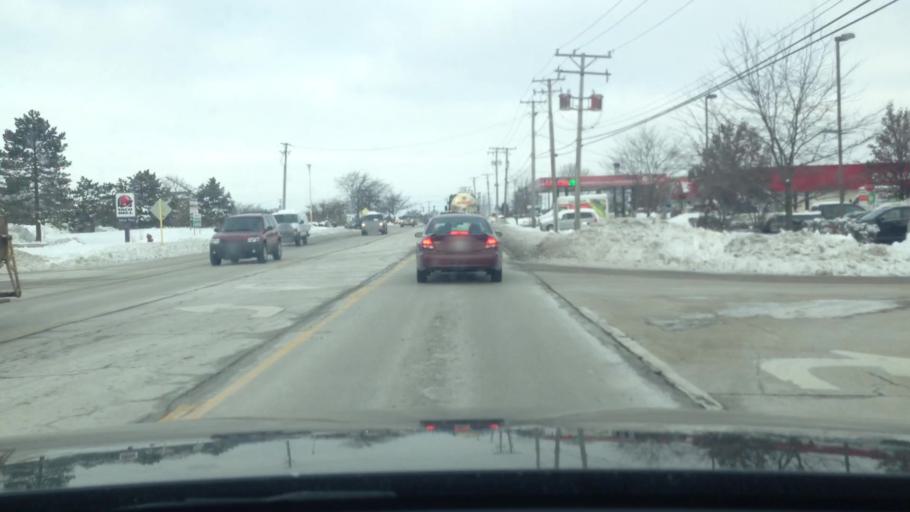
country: US
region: Illinois
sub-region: McHenry County
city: Woodstock
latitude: 42.3102
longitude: -88.4326
